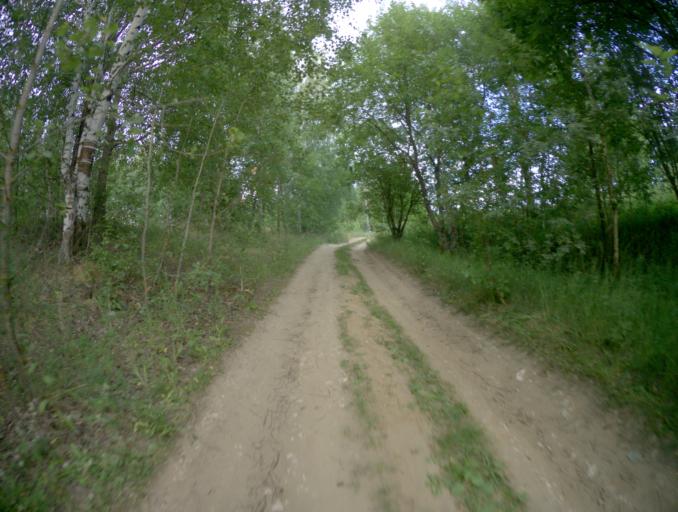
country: RU
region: Vladimir
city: Gorokhovets
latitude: 56.1918
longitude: 42.7653
